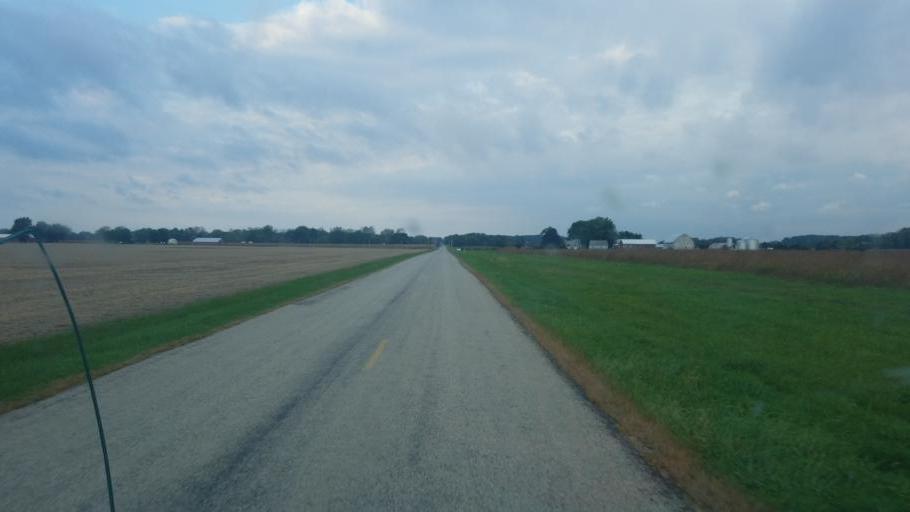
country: US
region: Ohio
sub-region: Marion County
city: Marion
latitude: 40.6737
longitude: -83.1340
